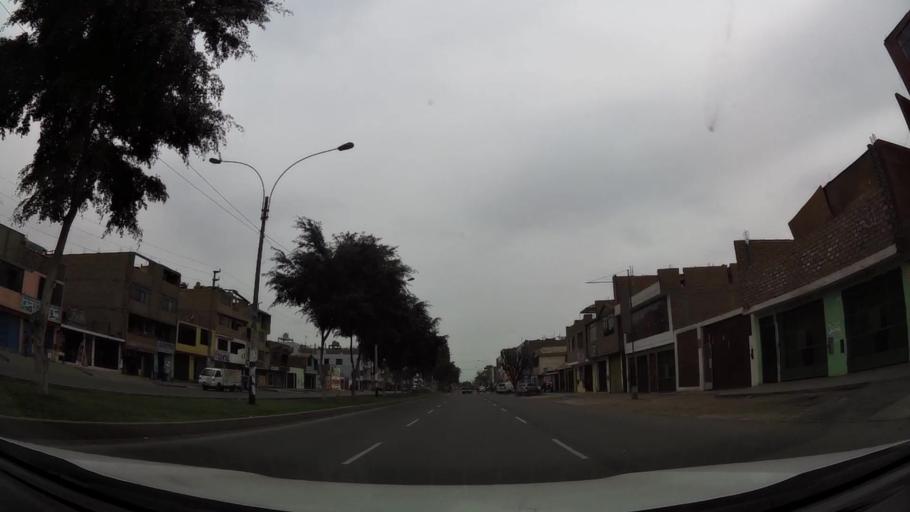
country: PE
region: Lima
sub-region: Lima
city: Independencia
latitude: -11.9738
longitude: -77.0821
